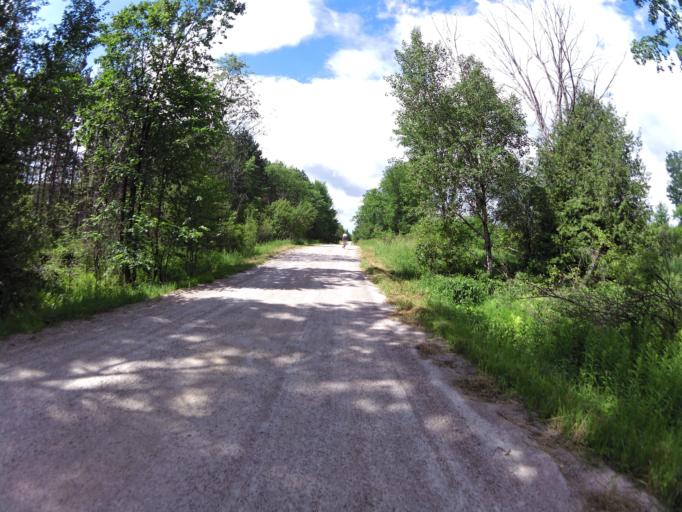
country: CA
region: Ontario
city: Perth
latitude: 45.0287
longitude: -76.5086
